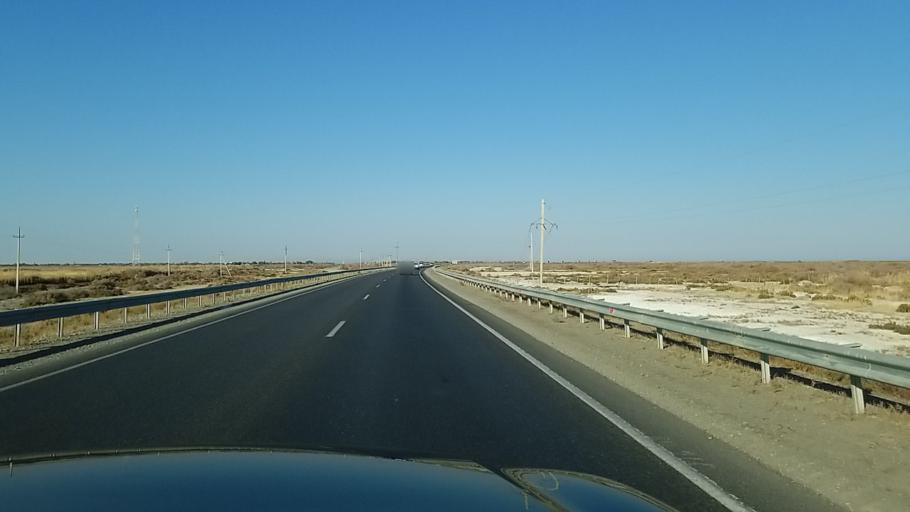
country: KZ
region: Qyzylorda
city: Terenozek
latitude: 44.8943
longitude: 65.0116
